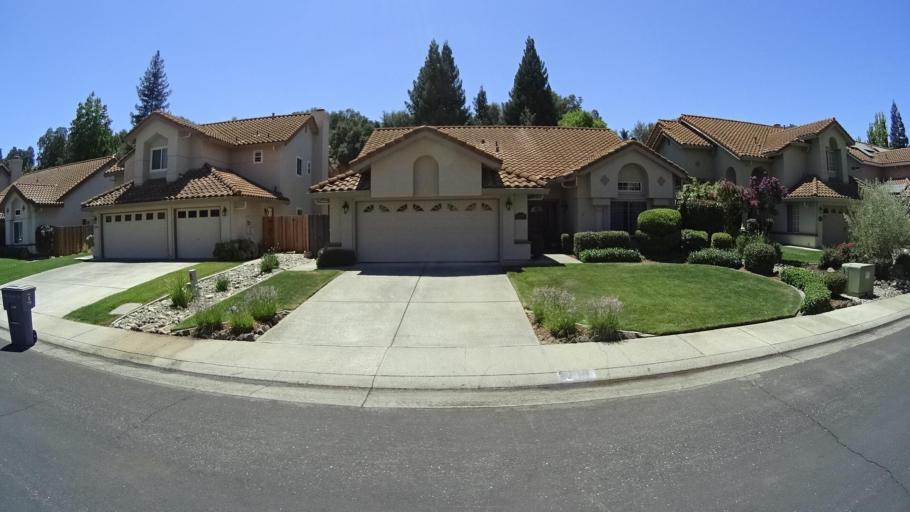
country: US
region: California
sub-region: Placer County
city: Rocklin
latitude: 38.8075
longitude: -121.2661
